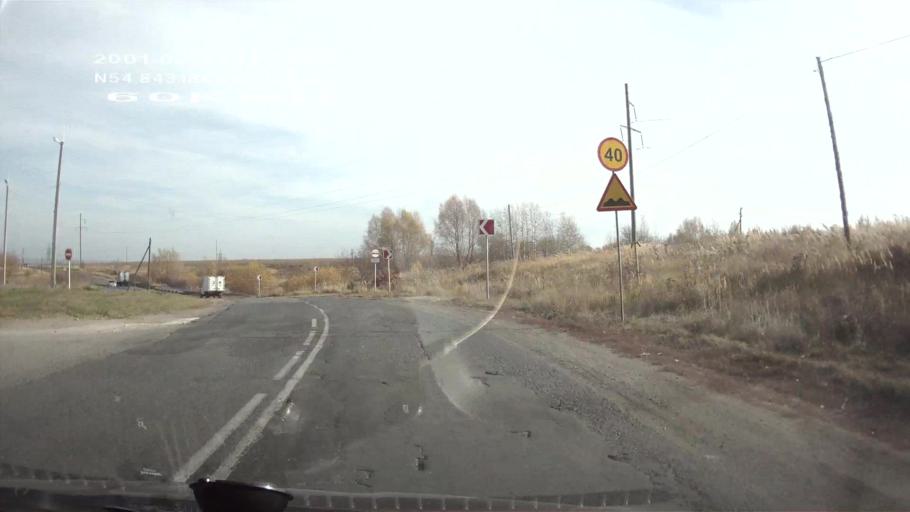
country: RU
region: Chuvashia
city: Alatyr'
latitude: 54.8432
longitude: 46.4747
